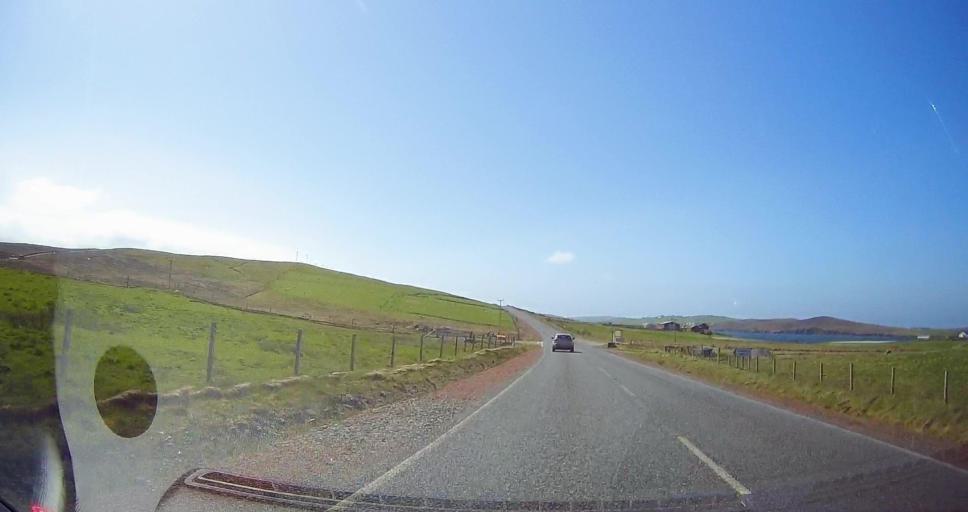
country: GB
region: Scotland
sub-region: Shetland Islands
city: Sandwick
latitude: 60.1183
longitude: -1.2909
